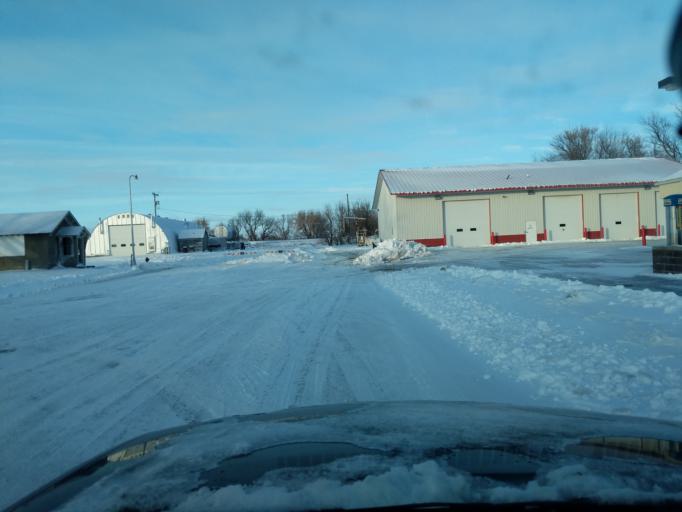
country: US
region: Minnesota
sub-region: Renville County
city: Olivia
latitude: 44.7769
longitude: -94.9956
